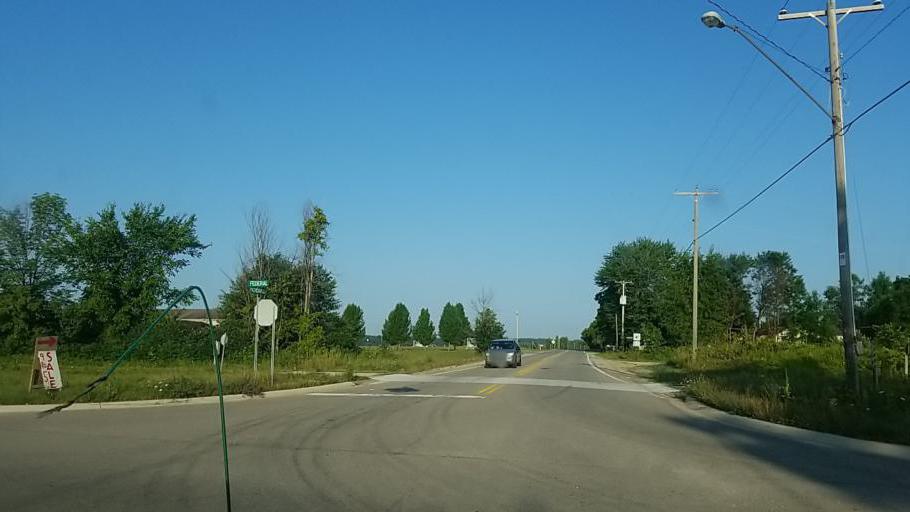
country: US
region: Michigan
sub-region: Montcalm County
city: Howard City
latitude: 43.3667
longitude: -85.4784
